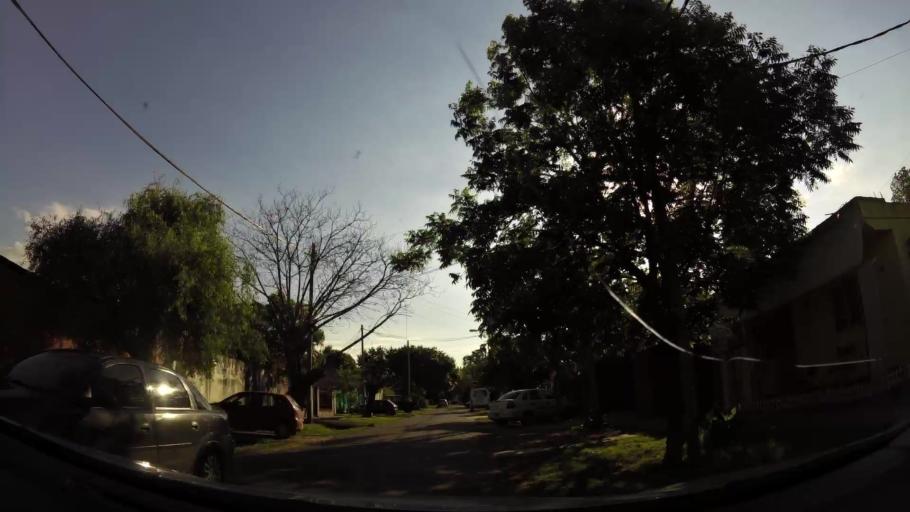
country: AR
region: Buenos Aires
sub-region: Partido de Tigre
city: Tigre
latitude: -34.4751
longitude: -58.6401
